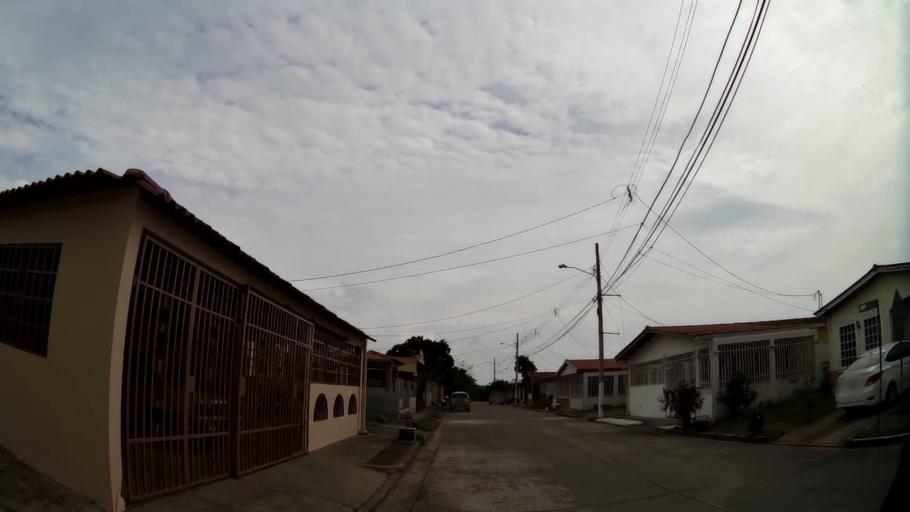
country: PA
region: Panama
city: Tocumen
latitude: 9.0456
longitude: -79.4021
